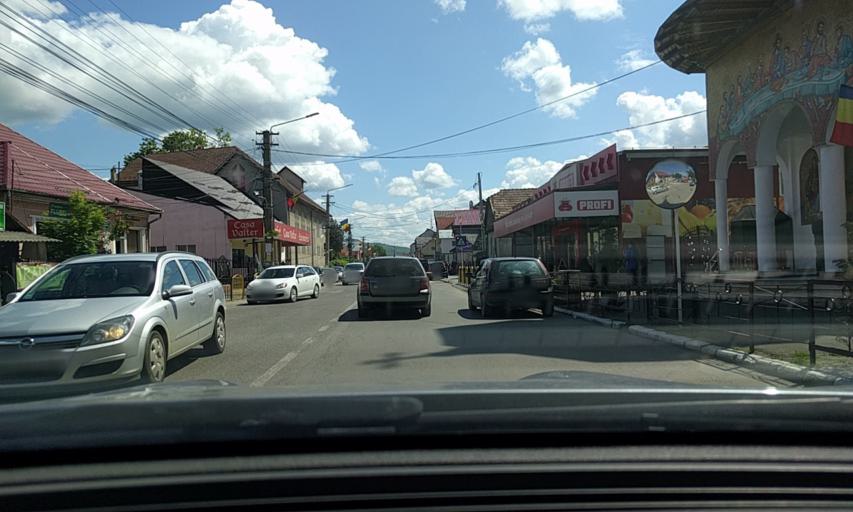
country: RO
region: Bistrita-Nasaud
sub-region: Oras Nasaud
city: Nasaud
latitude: 47.2834
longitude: 24.4128
